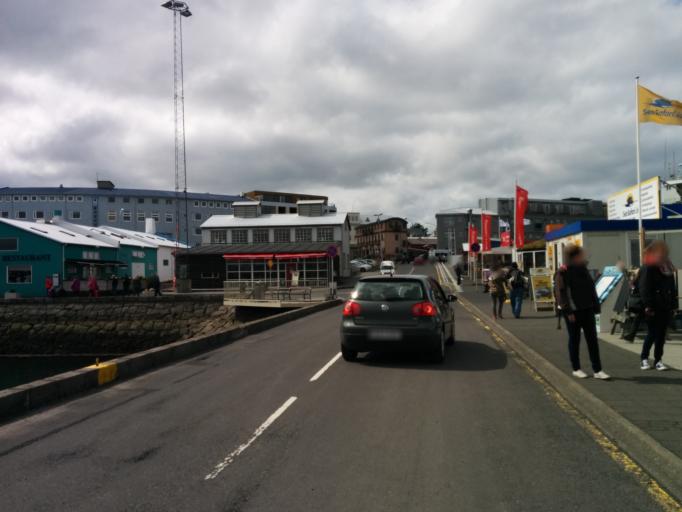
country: IS
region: Capital Region
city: Kopavogur
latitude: 64.1516
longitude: -21.9435
